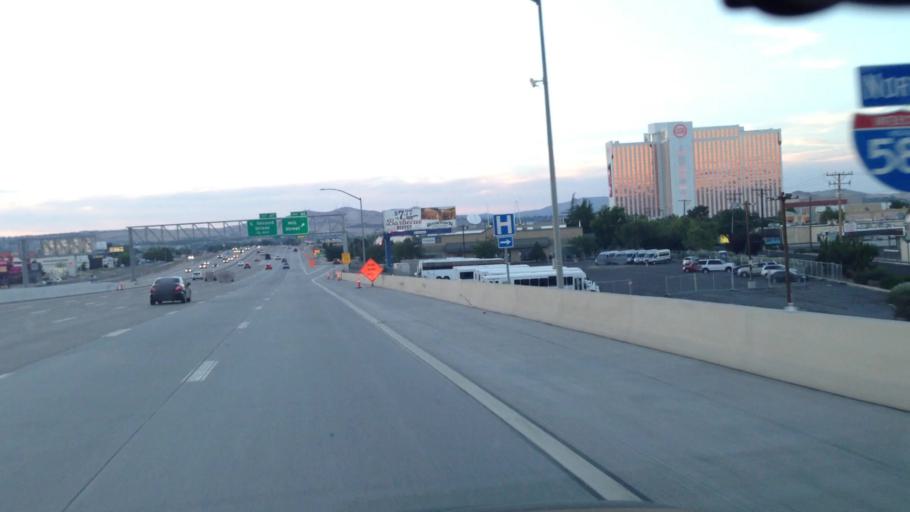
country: US
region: Nevada
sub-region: Washoe County
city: Sparks
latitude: 39.5137
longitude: -119.7812
